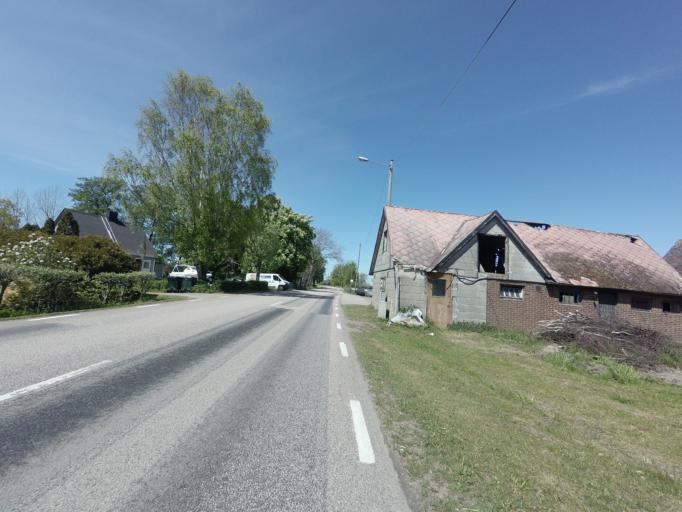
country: SE
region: Skane
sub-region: Helsingborg
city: Odakra
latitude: 56.1375
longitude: 12.6892
